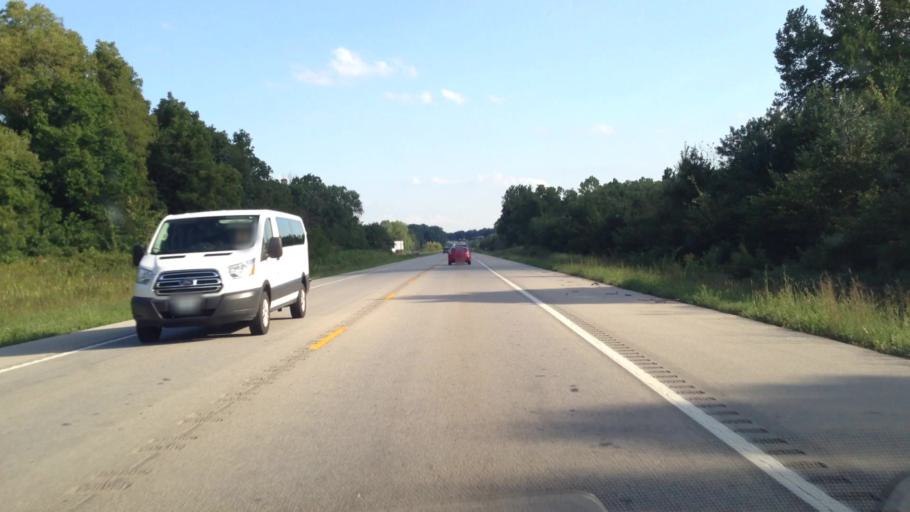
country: US
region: Missouri
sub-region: Jasper County
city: Carl Junction
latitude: 37.1556
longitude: -94.5274
